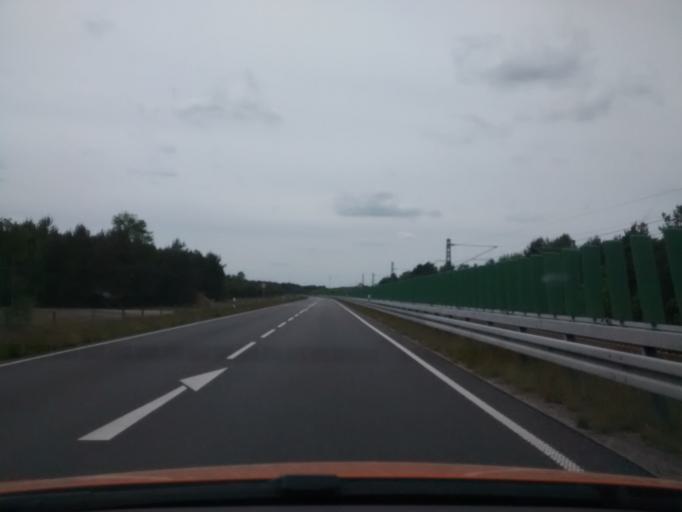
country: DE
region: Brandenburg
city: Luckenwalde
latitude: 52.0625
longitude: 13.1131
